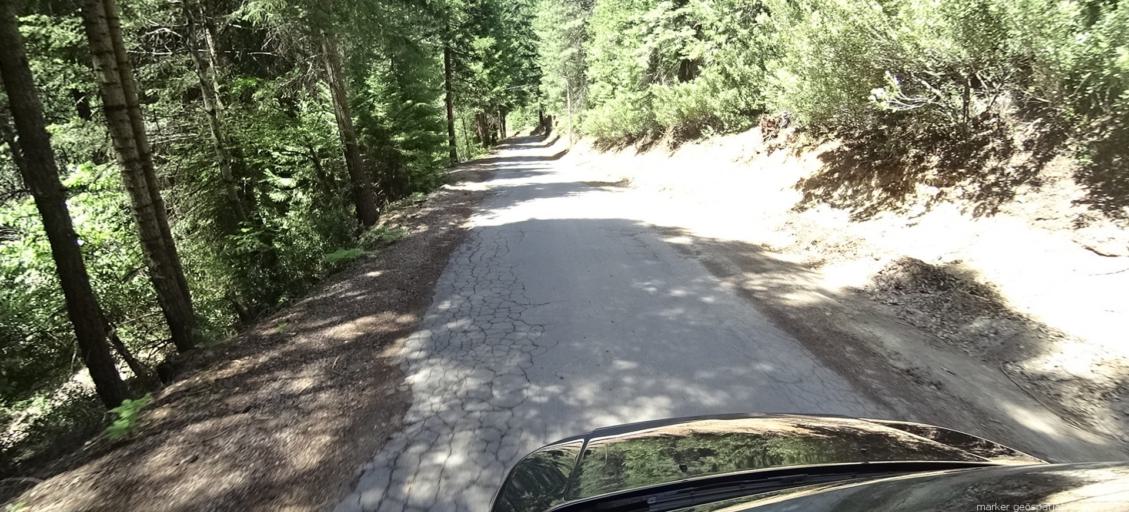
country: US
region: California
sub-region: Siskiyou County
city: Mount Shasta
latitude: 41.2725
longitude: -122.2853
